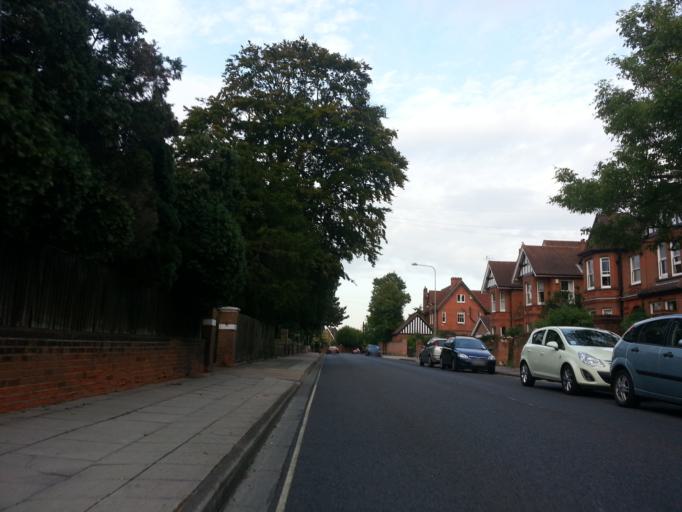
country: GB
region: England
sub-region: Suffolk
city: Ipswich
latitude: 52.0678
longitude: 1.1585
